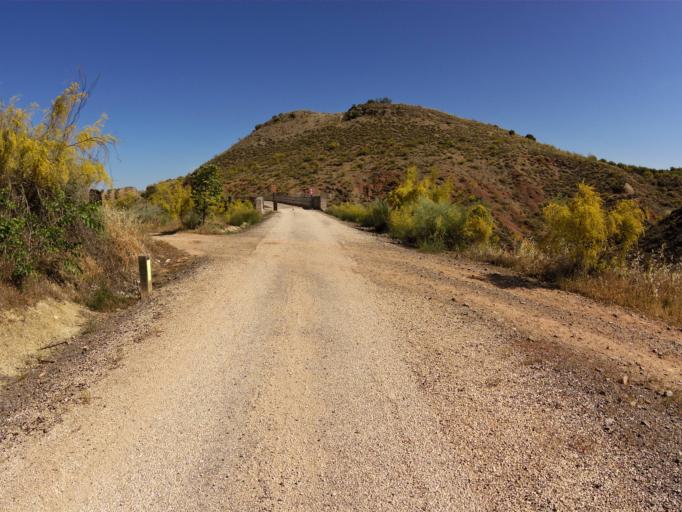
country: ES
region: Andalusia
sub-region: Provincia de Jaen
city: Alcaudete
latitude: 37.5983
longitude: -4.1562
